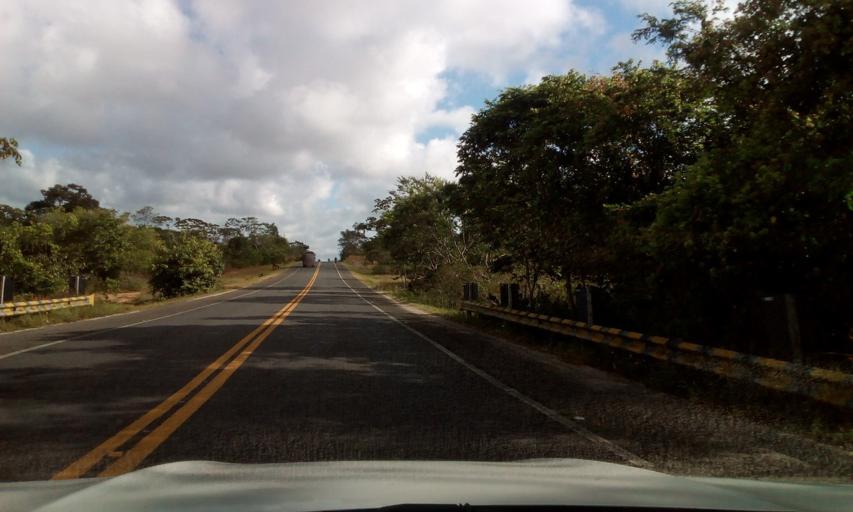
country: BR
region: Bahia
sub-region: Conde
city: Conde
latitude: -11.8060
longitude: -37.6305
